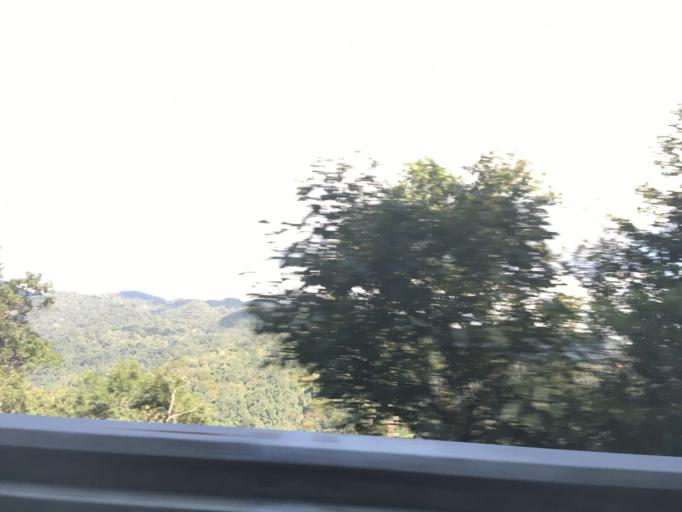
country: TW
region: Taiwan
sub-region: Yilan
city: Yilan
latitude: 24.7503
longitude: 121.6440
